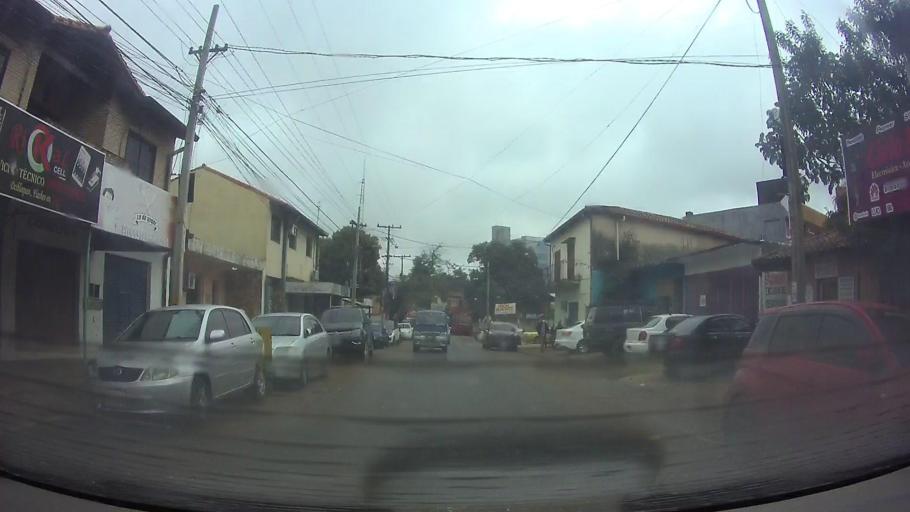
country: PY
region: Central
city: Fernando de la Mora
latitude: -25.3242
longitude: -57.5558
